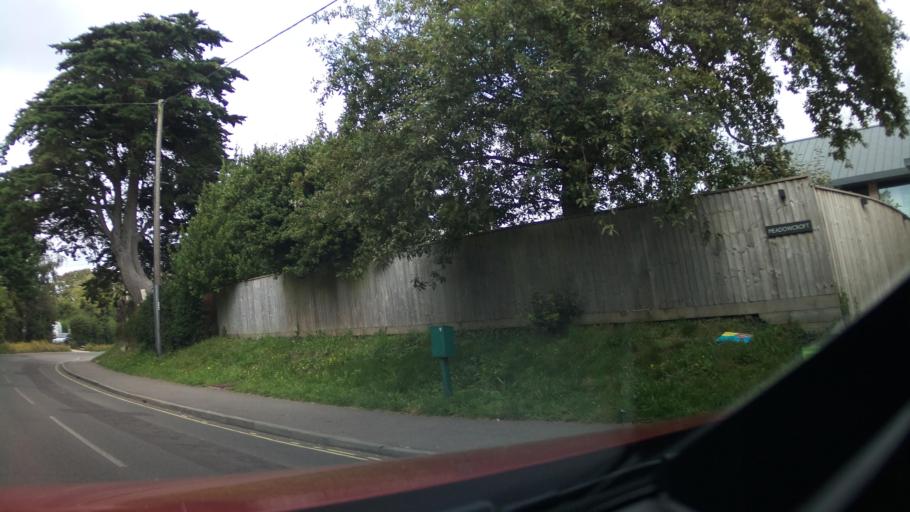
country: GB
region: England
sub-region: Hampshire
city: Milford on Sea
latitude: 50.7293
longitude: -1.5885
